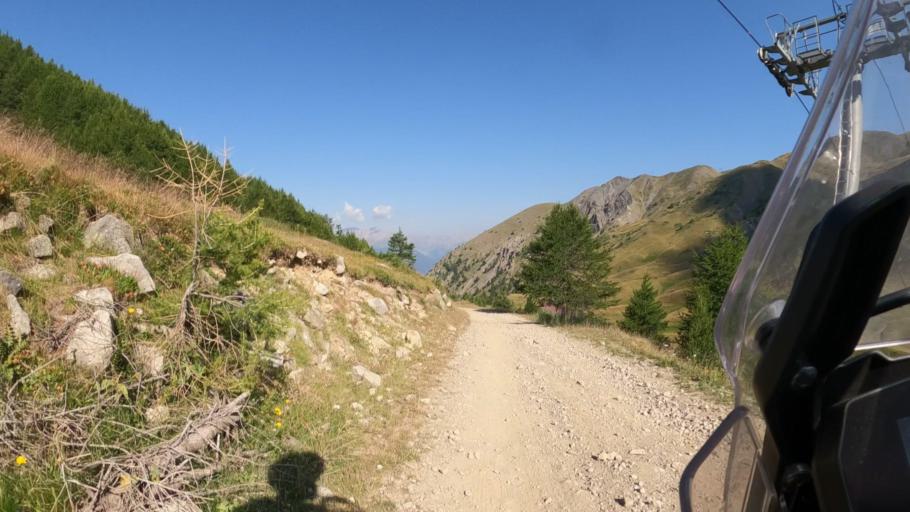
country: FR
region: Provence-Alpes-Cote d'Azur
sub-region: Departement des Hautes-Alpes
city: Guillestre
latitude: 44.5890
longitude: 6.6335
